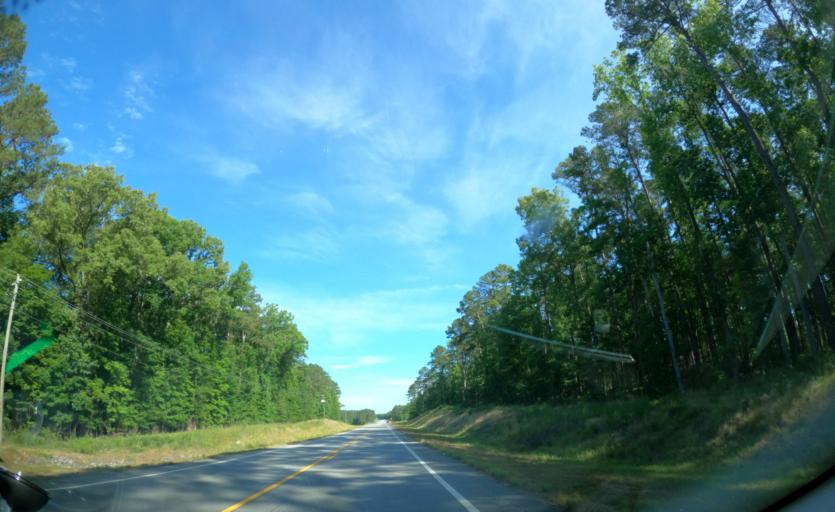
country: US
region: Georgia
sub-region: Columbia County
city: Appling
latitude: 33.6390
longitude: -82.3044
